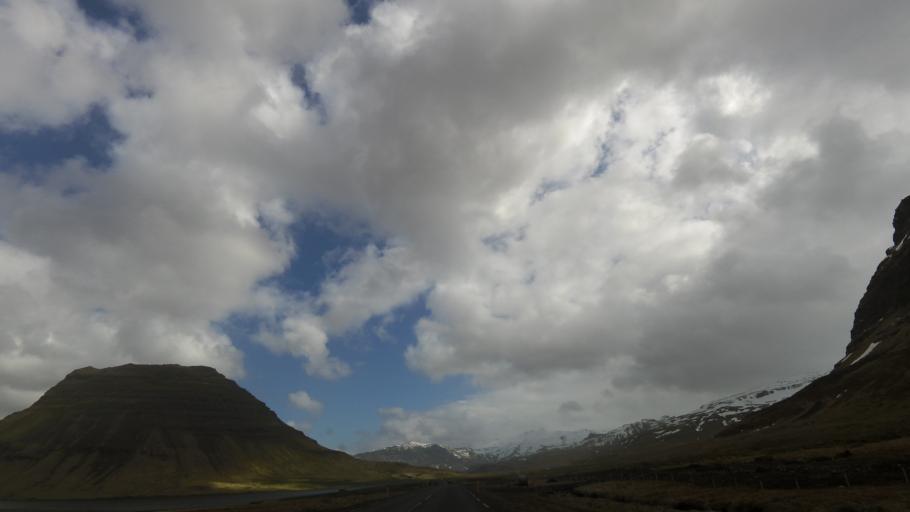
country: IS
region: West
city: Olafsvik
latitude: 64.9367
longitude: -23.3515
